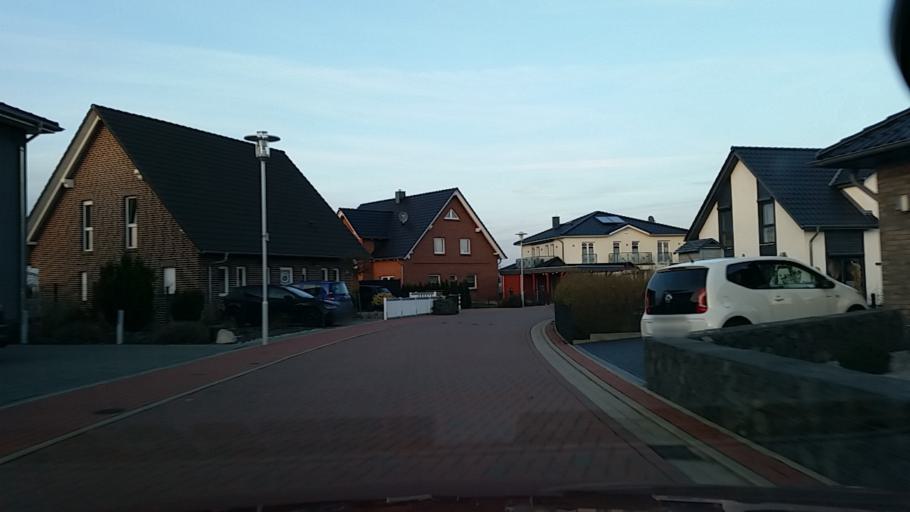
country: DE
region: Lower Saxony
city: Weyhausen
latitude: 52.4017
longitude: 10.7076
